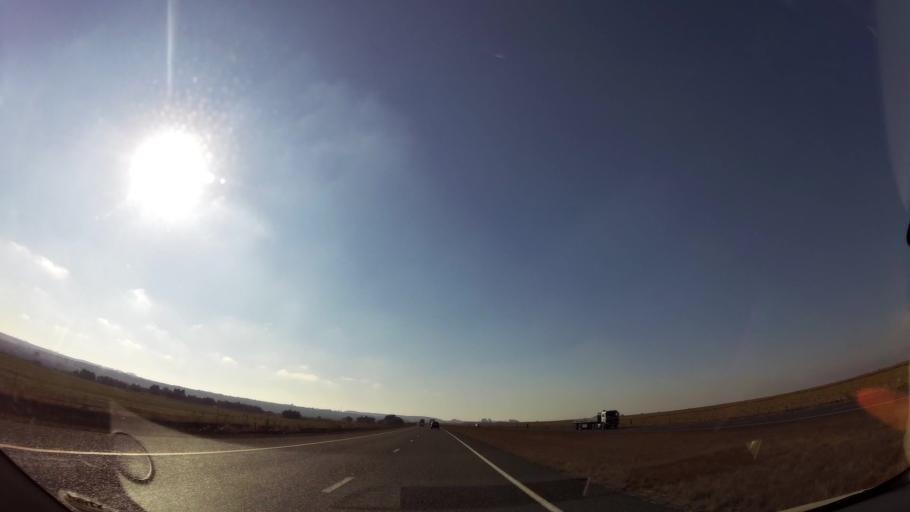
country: ZA
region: Mpumalanga
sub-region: Nkangala District Municipality
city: Delmas
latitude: -26.0191
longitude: 28.9275
